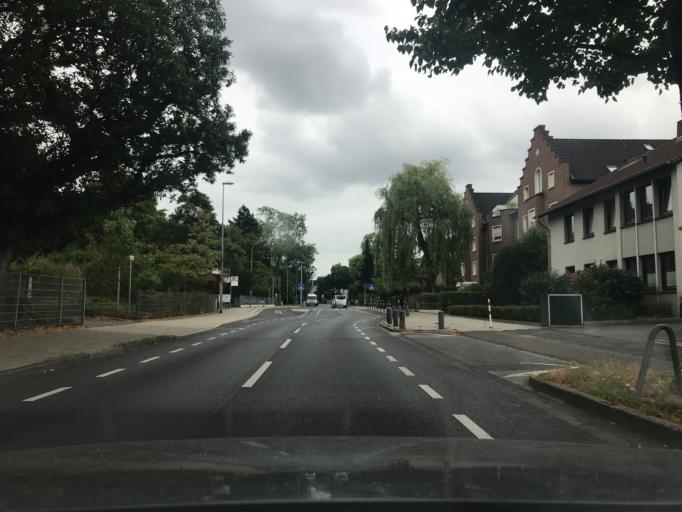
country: DE
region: North Rhine-Westphalia
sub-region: Regierungsbezirk Dusseldorf
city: Hilden
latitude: 51.1740
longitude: 6.9279
